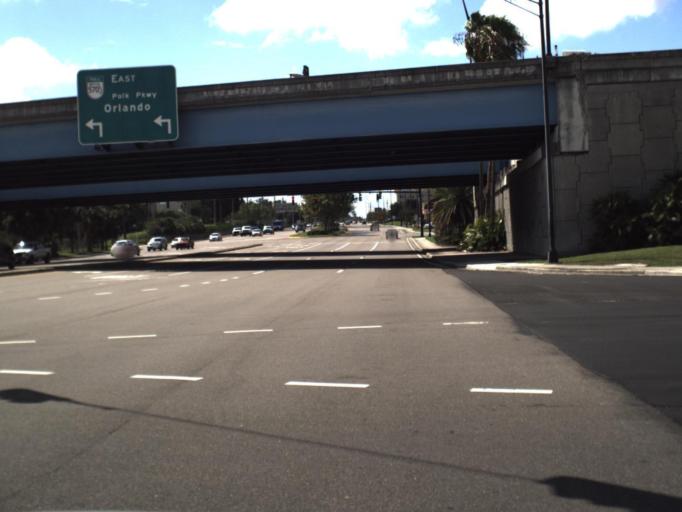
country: US
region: Florida
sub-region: Polk County
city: Medulla
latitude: 27.9968
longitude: -81.9572
